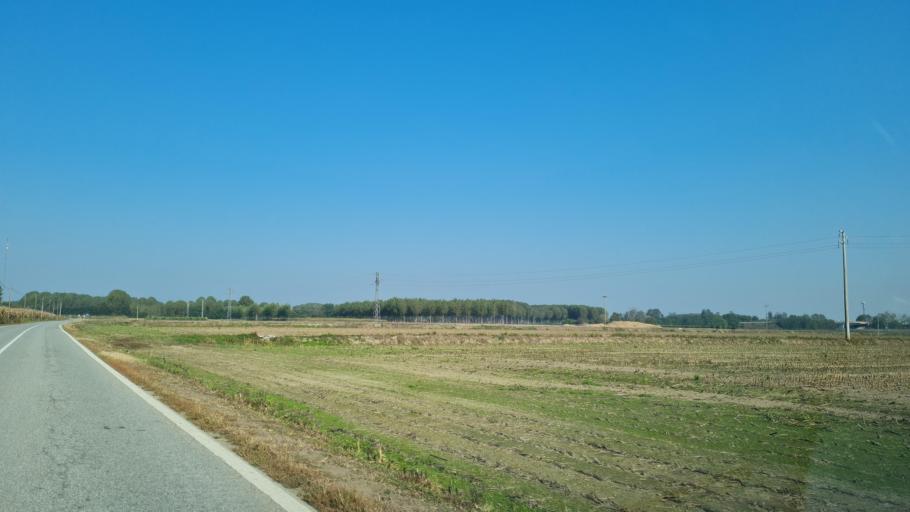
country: IT
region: Piedmont
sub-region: Provincia di Novara
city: Landiona
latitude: 45.4910
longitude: 8.4322
